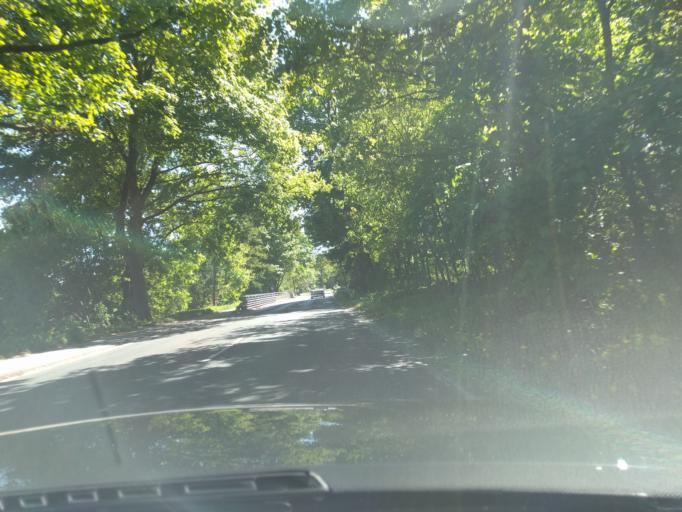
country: DE
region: Lower Saxony
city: Seevetal
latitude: 53.3938
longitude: 10.0133
